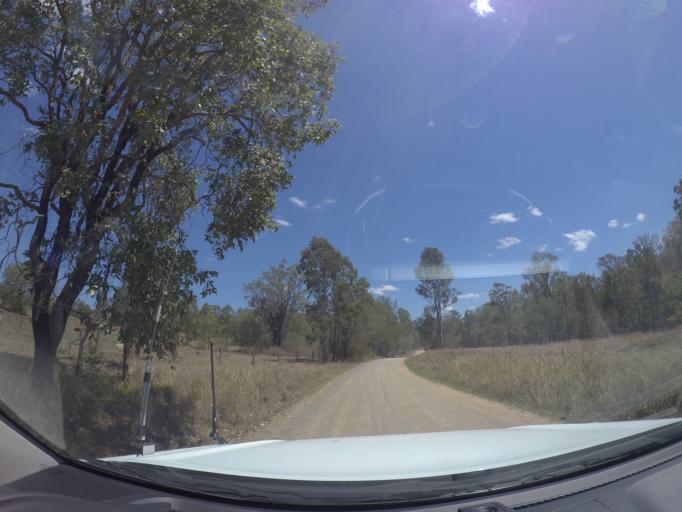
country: AU
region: Queensland
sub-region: Logan
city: North Maclean
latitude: -27.8270
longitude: 152.8628
